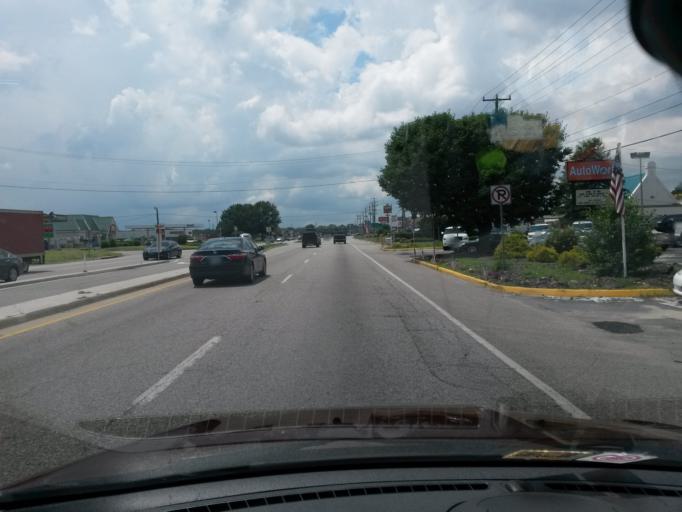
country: US
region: Virginia
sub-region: Chesterfield County
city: Chester
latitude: 37.3549
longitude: -77.4090
